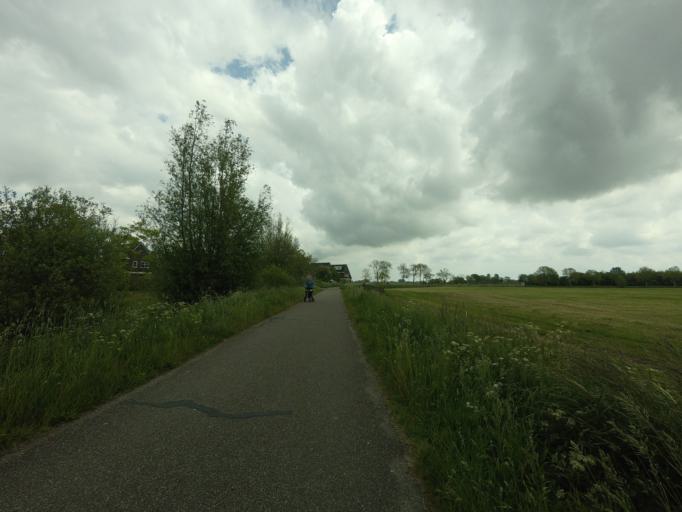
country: NL
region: Friesland
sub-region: Gemeente Littenseradiel
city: Wommels
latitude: 53.1072
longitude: 5.5954
